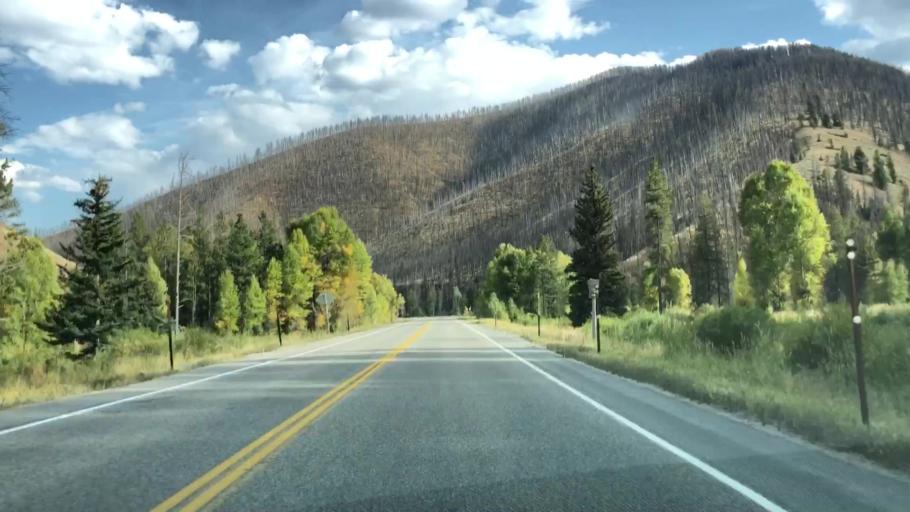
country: US
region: Wyoming
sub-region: Teton County
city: Hoback
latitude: 43.2504
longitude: -110.4960
